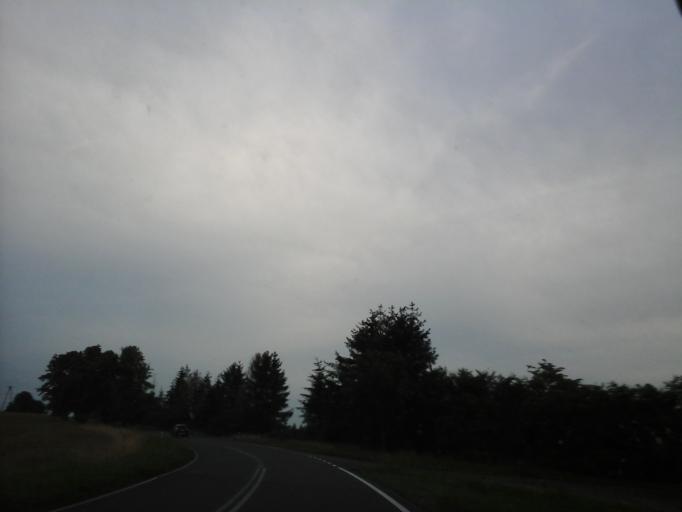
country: PL
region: West Pomeranian Voivodeship
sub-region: Powiat stargardzki
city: Stargard Szczecinski
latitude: 53.3597
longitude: 15.0617
